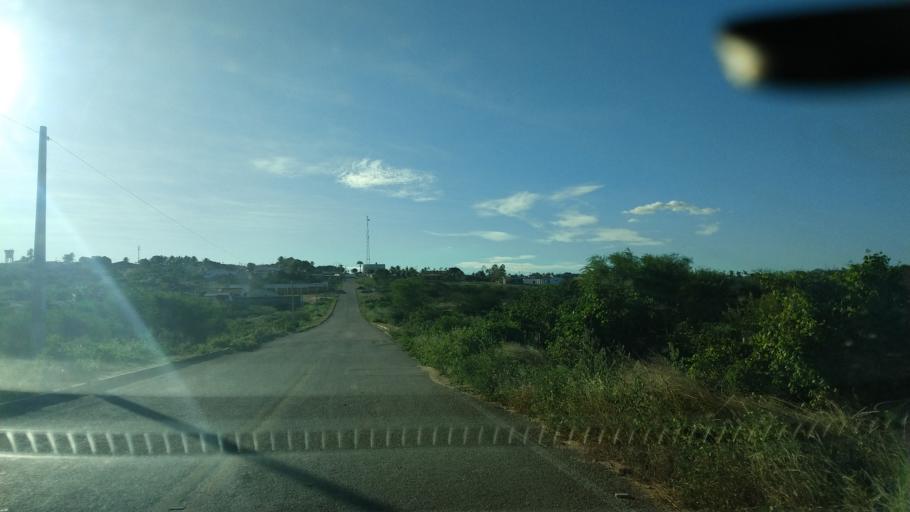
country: BR
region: Rio Grande do Norte
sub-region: Tangara
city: Tangara
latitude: -6.2061
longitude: -35.7962
